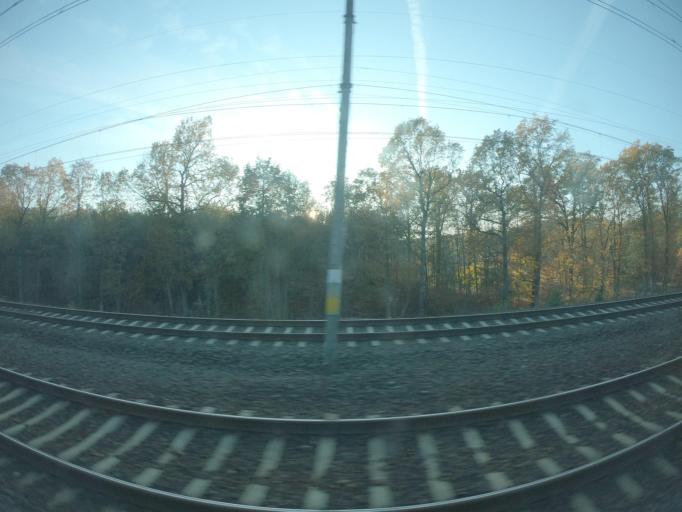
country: PL
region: Lubusz
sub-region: Powiat slubicki
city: Rzepin
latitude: 52.3220
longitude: 14.8491
